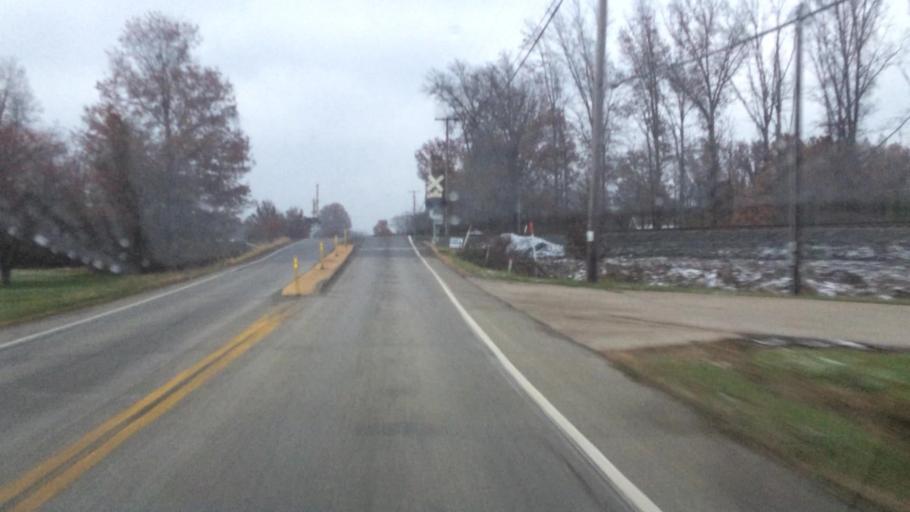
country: US
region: Ohio
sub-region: Cuyahoga County
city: Olmsted Falls
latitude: 41.3508
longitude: -81.9132
